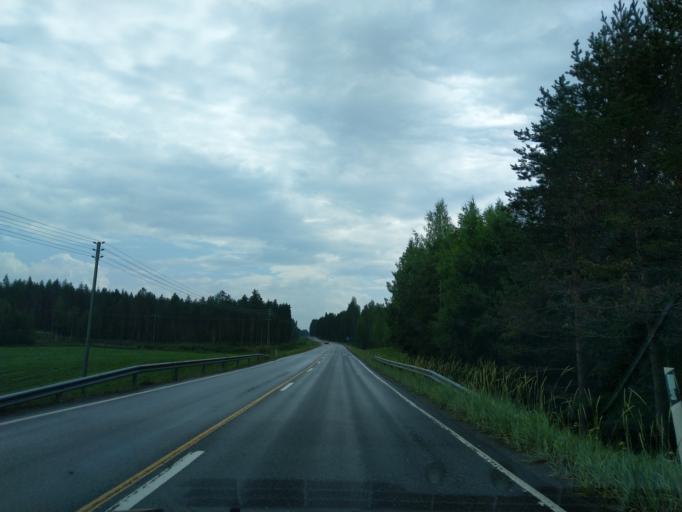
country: FI
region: Southern Savonia
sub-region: Savonlinna
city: Punkaharju
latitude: 61.6599
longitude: 29.4170
